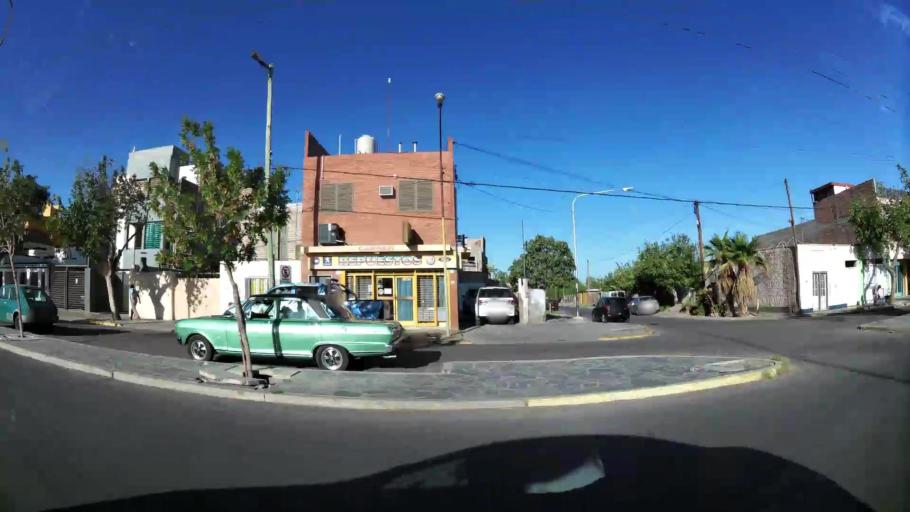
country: AR
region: San Juan
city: San Juan
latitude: -31.5458
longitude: -68.5204
